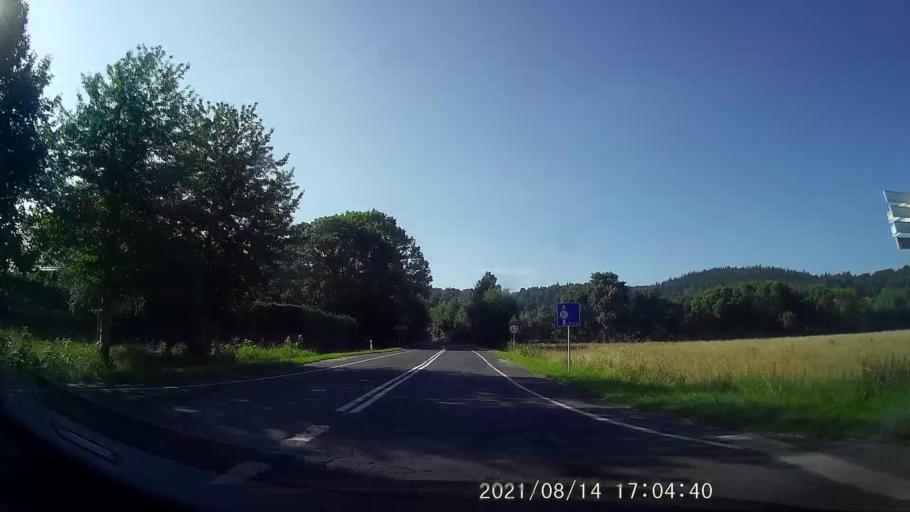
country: PL
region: Lower Silesian Voivodeship
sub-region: Powiat jeleniogorski
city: Kowary
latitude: 50.8030
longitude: 15.8374
